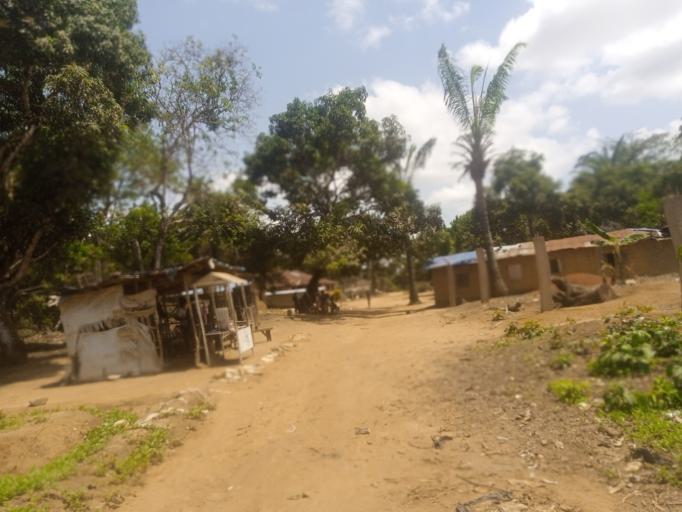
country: SL
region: Western Area
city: Waterloo
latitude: 8.3169
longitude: -13.0048
